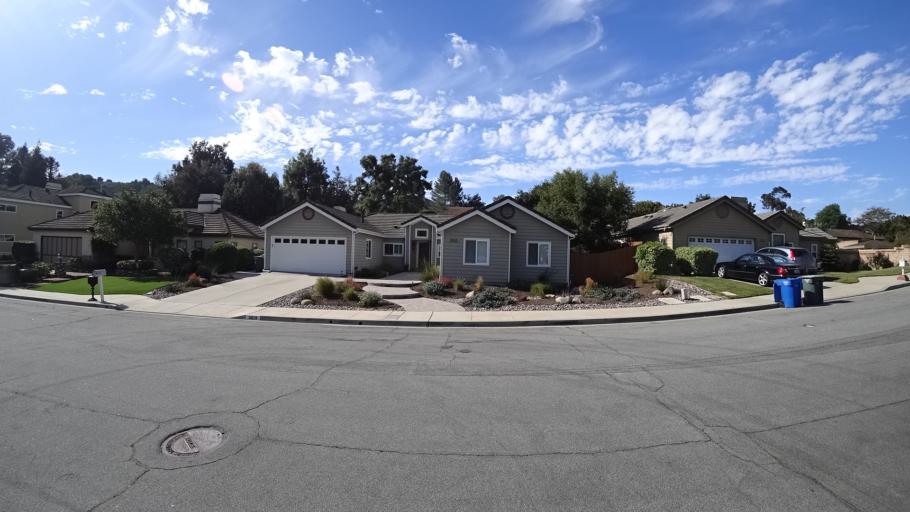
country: US
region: California
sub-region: Ventura County
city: Casa Conejo
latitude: 34.1736
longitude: -118.9404
